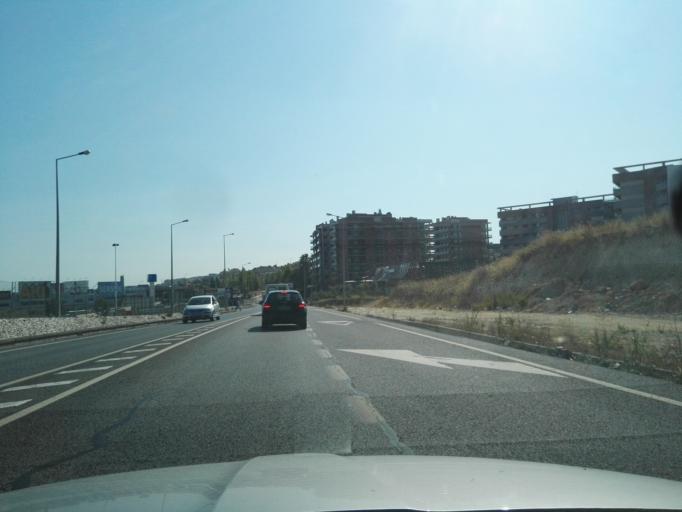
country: PT
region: Lisbon
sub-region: Vila Franca de Xira
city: Vialonga
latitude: 38.8904
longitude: -9.0443
